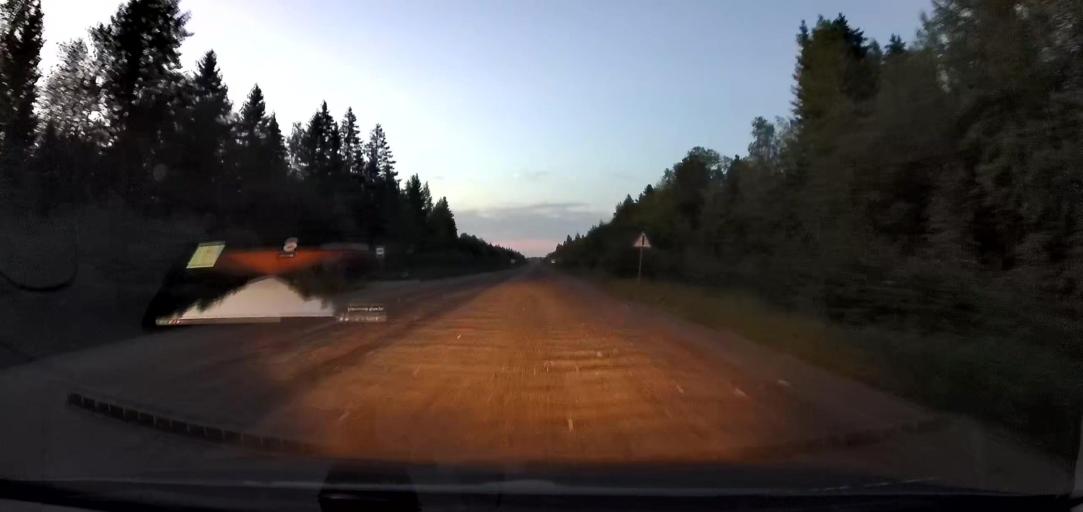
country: RU
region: Arkhangelskaya
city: Kholmogory
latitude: 64.3290
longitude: 41.4281
